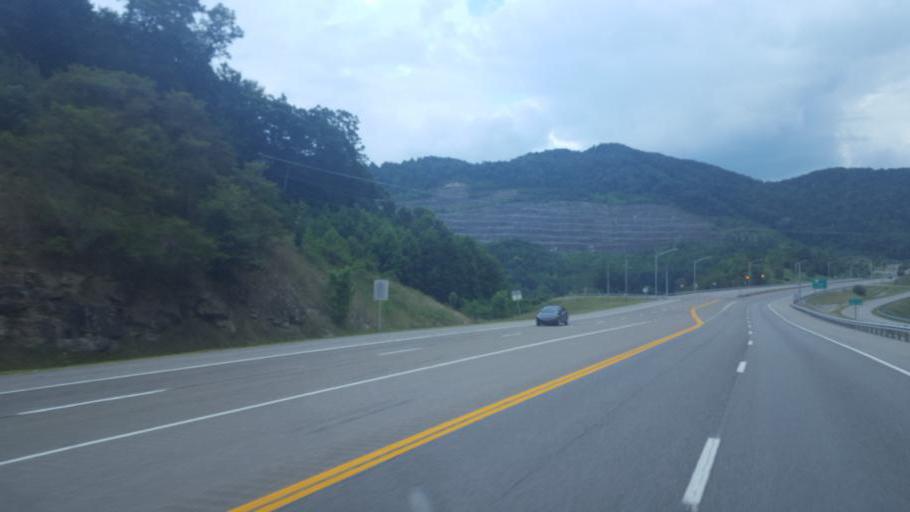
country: US
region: Kentucky
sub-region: Letcher County
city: Jenkins
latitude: 37.1665
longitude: -82.6465
